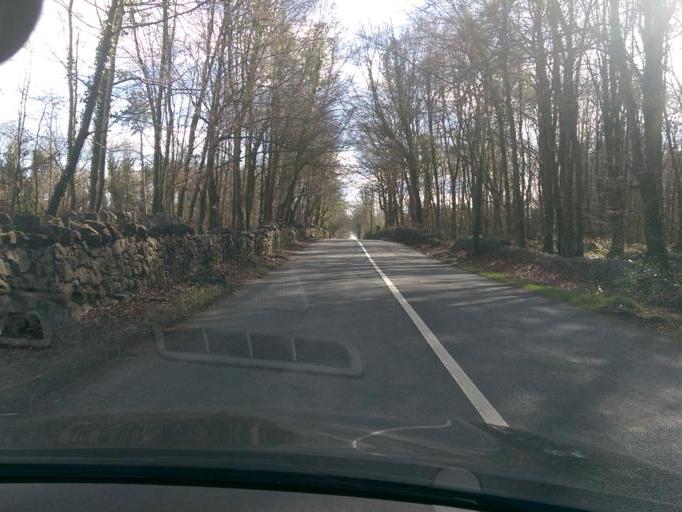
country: IE
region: Connaught
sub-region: County Galway
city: Athenry
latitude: 53.3350
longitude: -8.7705
